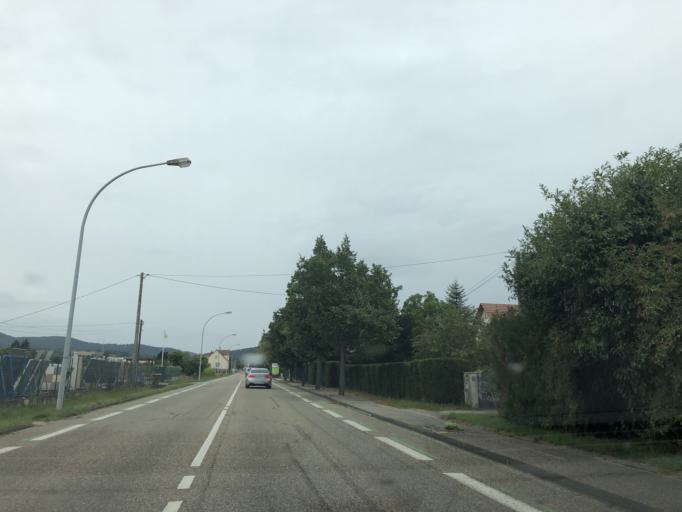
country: FR
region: Alsace
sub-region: Departement du Bas-Rhin
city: Wissembourg
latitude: 49.0266
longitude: 7.9691
